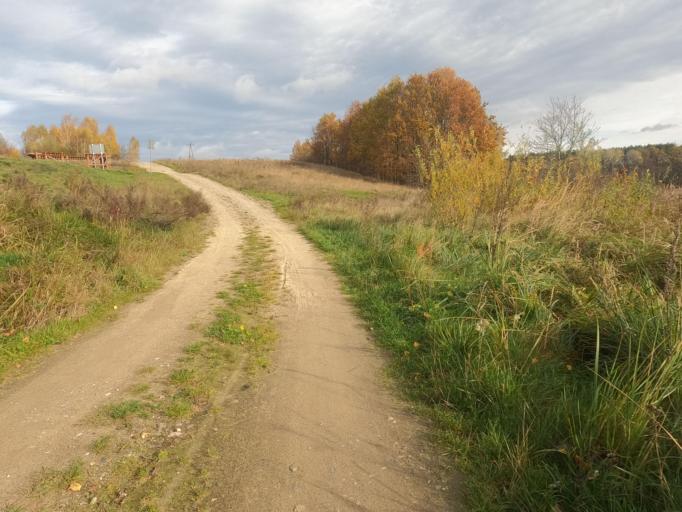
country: PL
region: Pomeranian Voivodeship
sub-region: Powiat starogardzki
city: Starogard Gdanski
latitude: 53.9720
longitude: 18.4811
